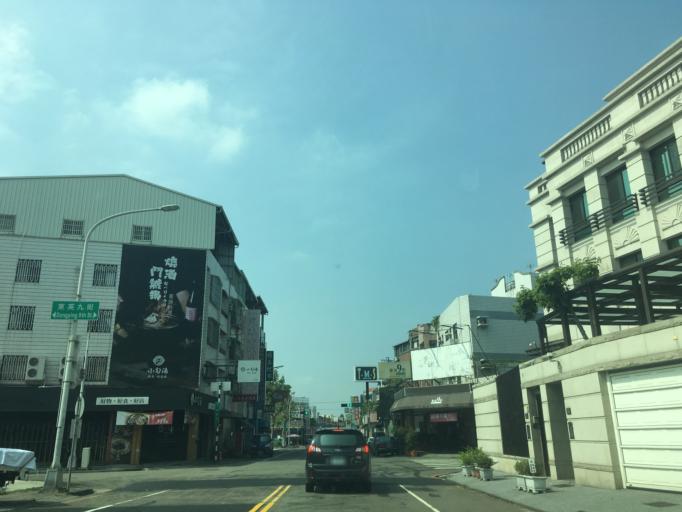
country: TW
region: Taiwan
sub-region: Taichung City
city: Taichung
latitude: 24.1425
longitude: 120.7087
